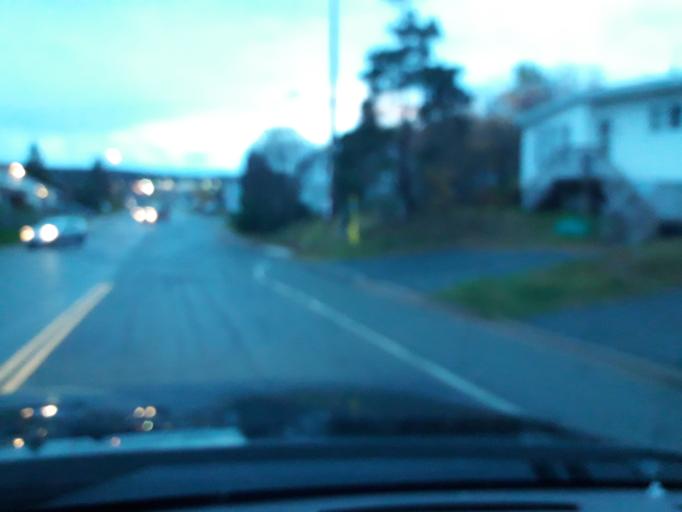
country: CA
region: Newfoundland and Labrador
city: St. John's
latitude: 47.5659
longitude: -52.7528
